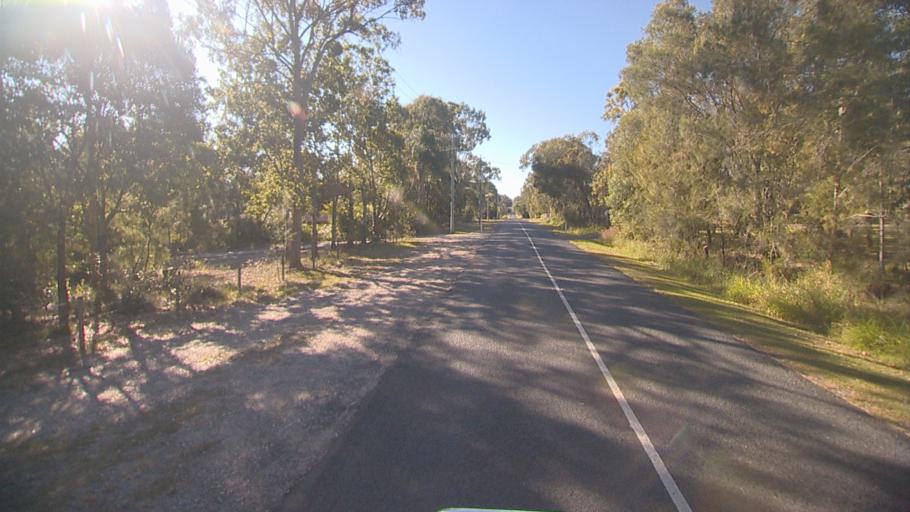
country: AU
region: Queensland
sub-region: Logan
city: Logan Reserve
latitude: -27.7386
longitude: 153.1030
